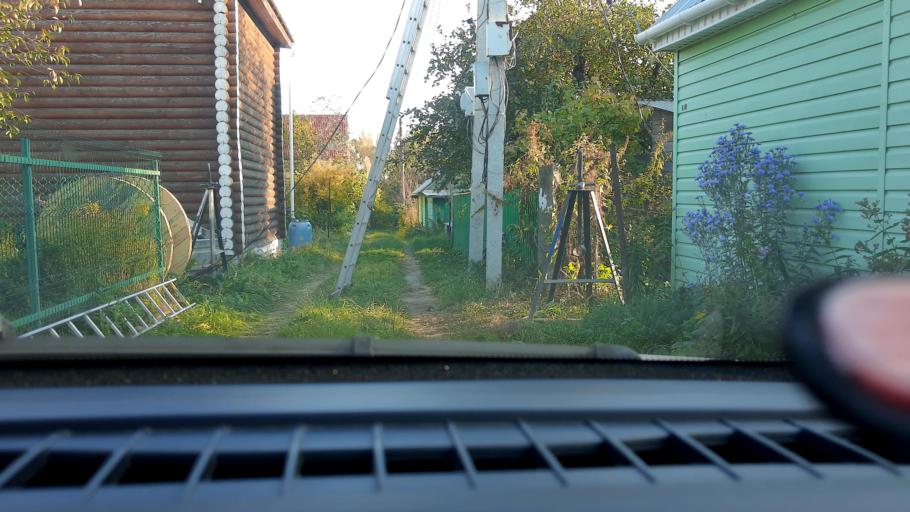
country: RU
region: Nizjnij Novgorod
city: Afonino
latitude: 56.2206
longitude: 44.0843
